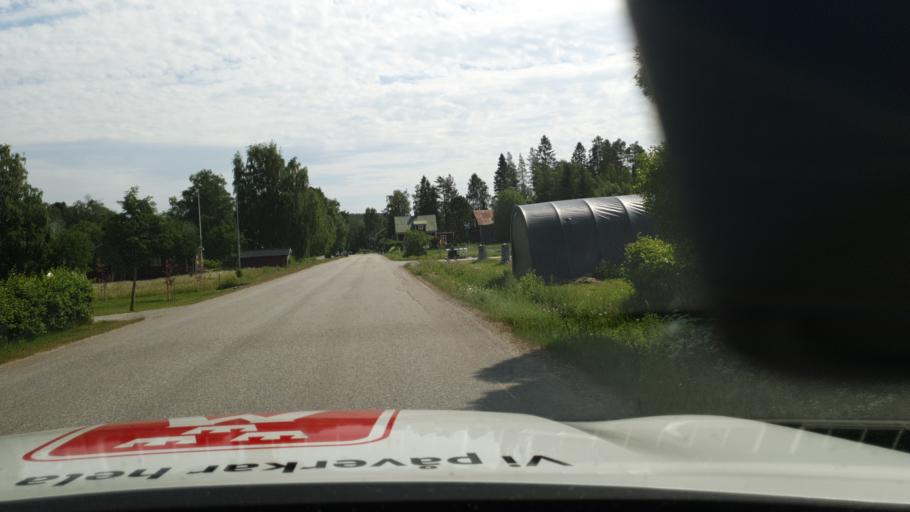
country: SE
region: Vaesterbotten
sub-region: Umea Kommun
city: Ersmark
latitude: 64.2557
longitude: 20.2391
